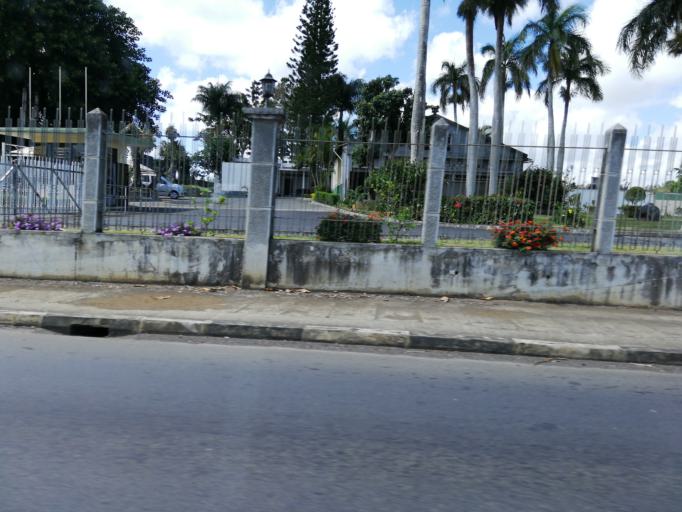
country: MU
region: Plaines Wilhems
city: Ebene
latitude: -20.2512
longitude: 57.4924
